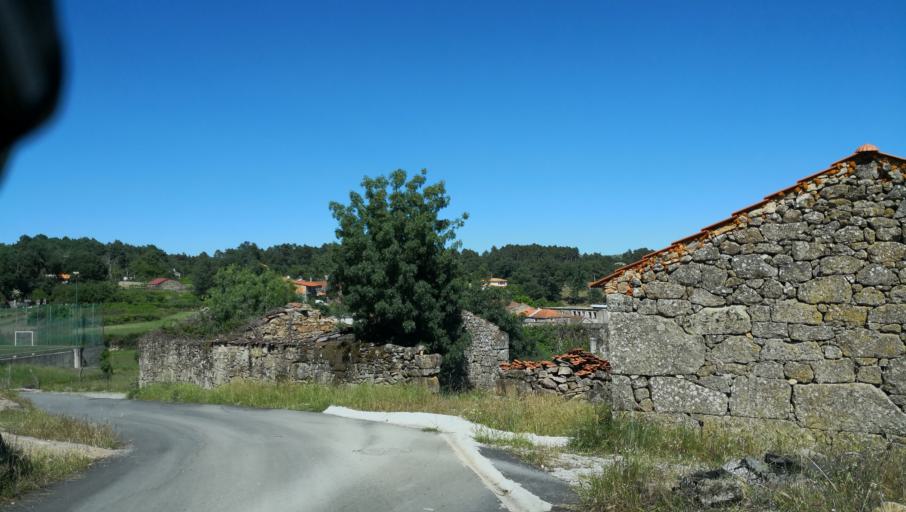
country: PT
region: Vila Real
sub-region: Vila Real
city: Vila Real
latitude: 41.2922
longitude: -7.6803
